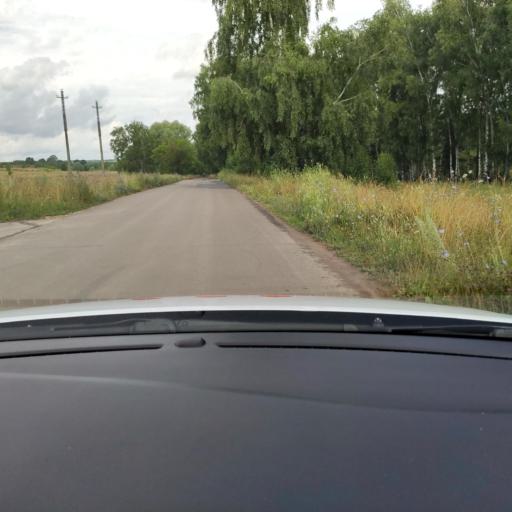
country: RU
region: Tatarstan
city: Staroye Arakchino
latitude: 55.8907
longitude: 49.0302
